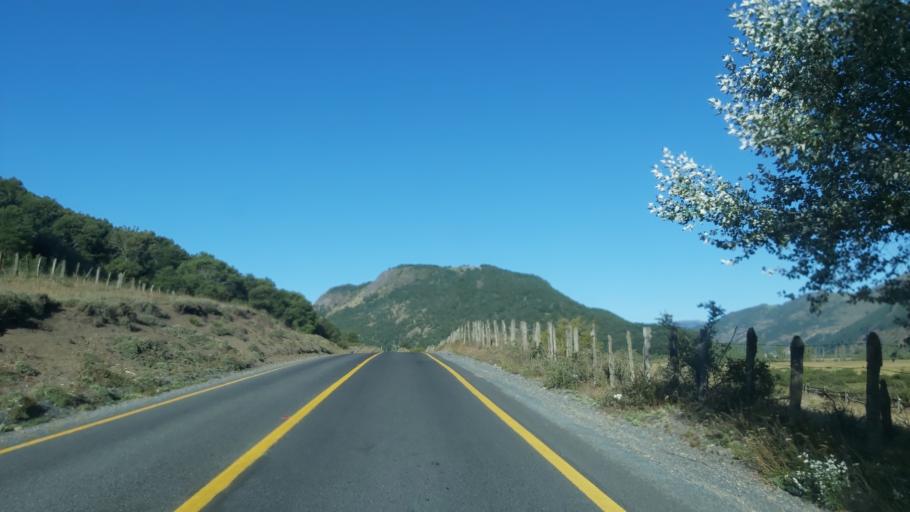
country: AR
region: Neuquen
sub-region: Departamento de Loncopue
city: Loncopue
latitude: -38.4454
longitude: -71.3516
